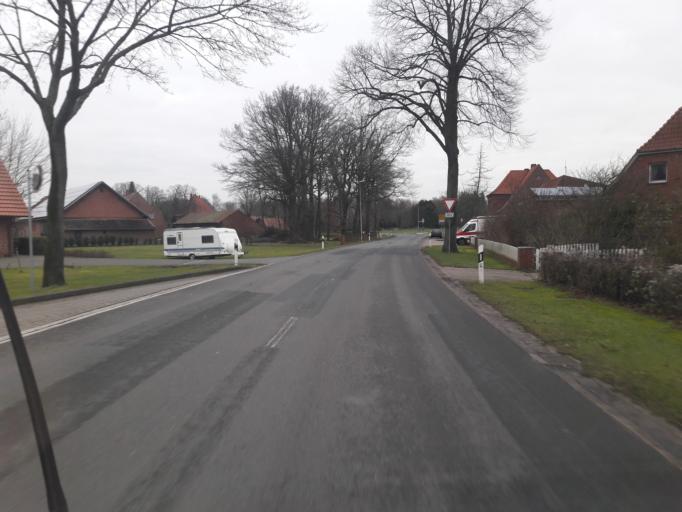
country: DE
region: Lower Saxony
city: Warmsen
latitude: 52.4504
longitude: 8.8524
